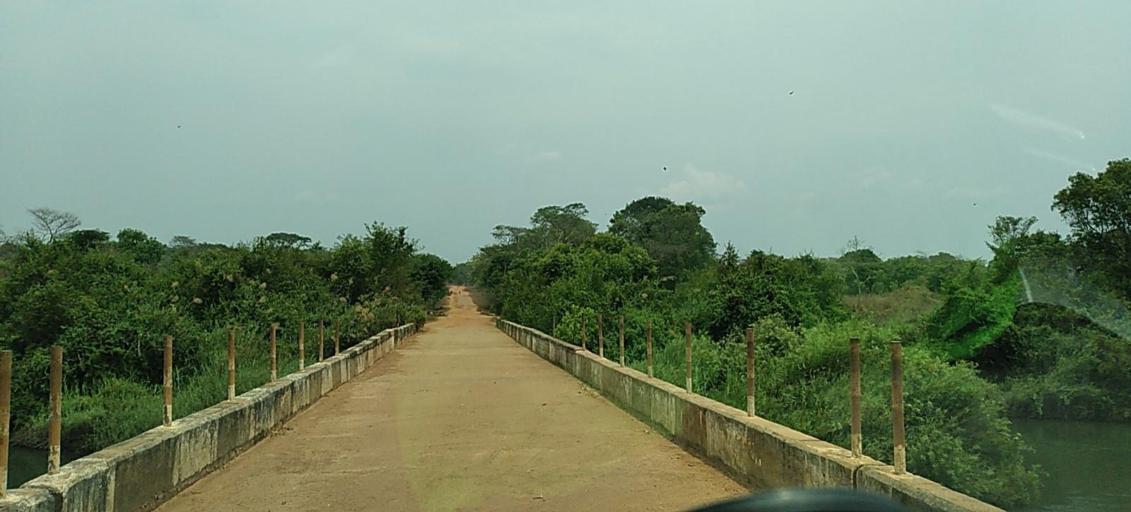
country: ZM
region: North-Western
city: Solwezi
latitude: -12.7958
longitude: 26.5328
